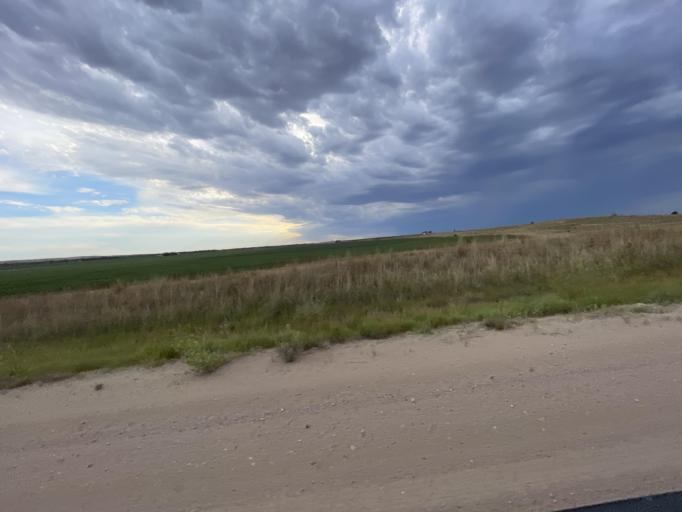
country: US
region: Nebraska
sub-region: Red Willow County
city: McCook
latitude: 40.2413
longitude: -100.7603
